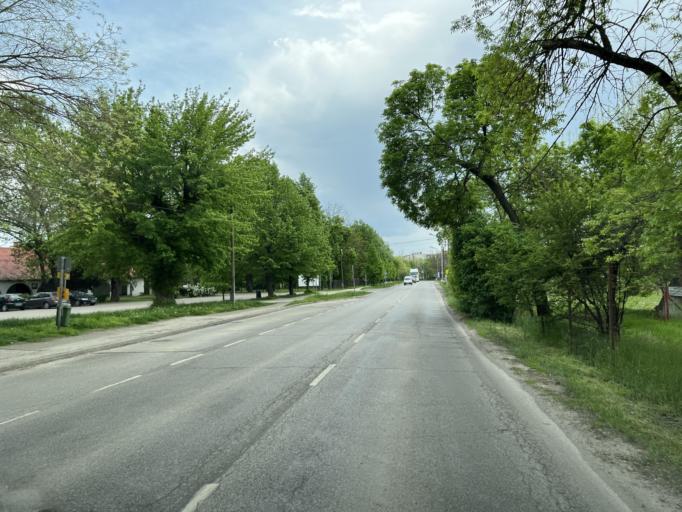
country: HU
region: Pest
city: Nagykoros
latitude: 47.0441
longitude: 19.7843
